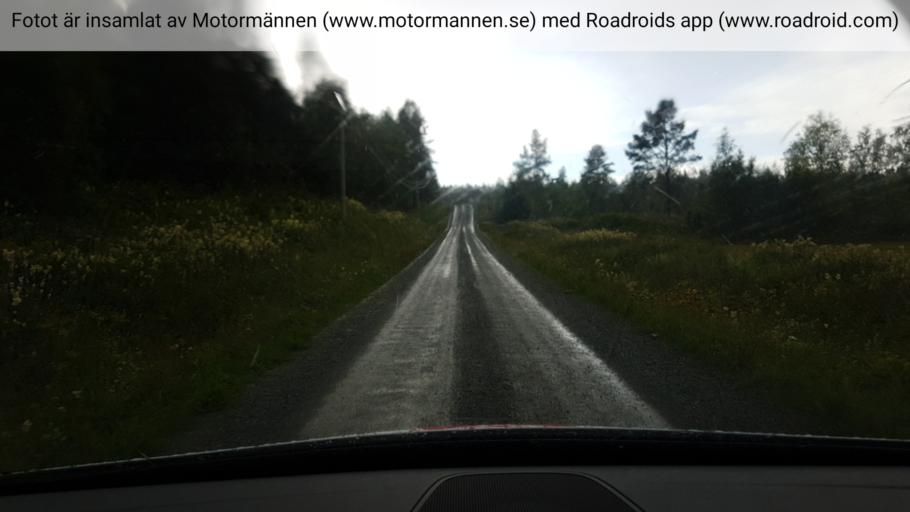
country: SE
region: Jaemtland
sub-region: OEstersunds Kommun
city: Brunflo
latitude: 63.0473
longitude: 14.7044
